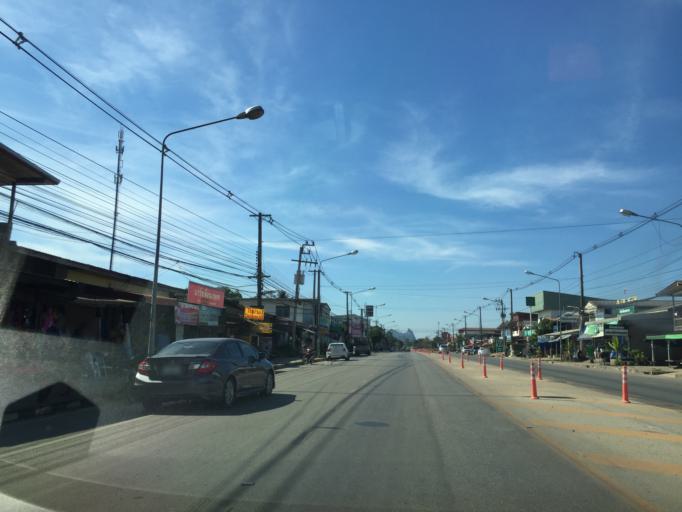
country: TH
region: Changwat Nong Bua Lamphu
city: Na Wang
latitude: 17.3230
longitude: 102.0845
